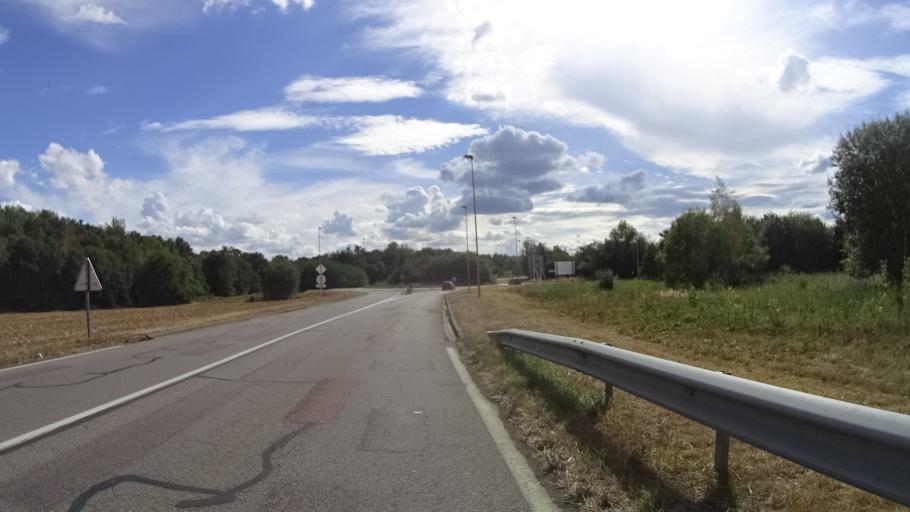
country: FR
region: Bourgogne
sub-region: Departement de la Cote-d'Or
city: Seurre
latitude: 47.0364
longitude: 5.1808
